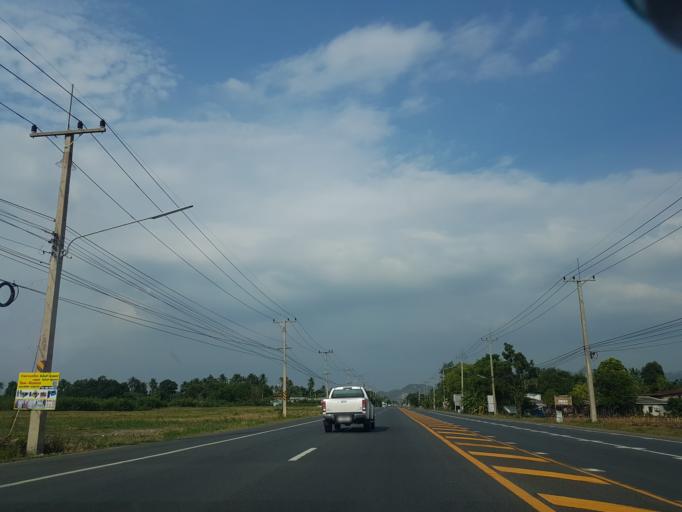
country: TH
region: Sara Buri
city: Ban Mo
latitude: 14.6507
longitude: 100.7615
